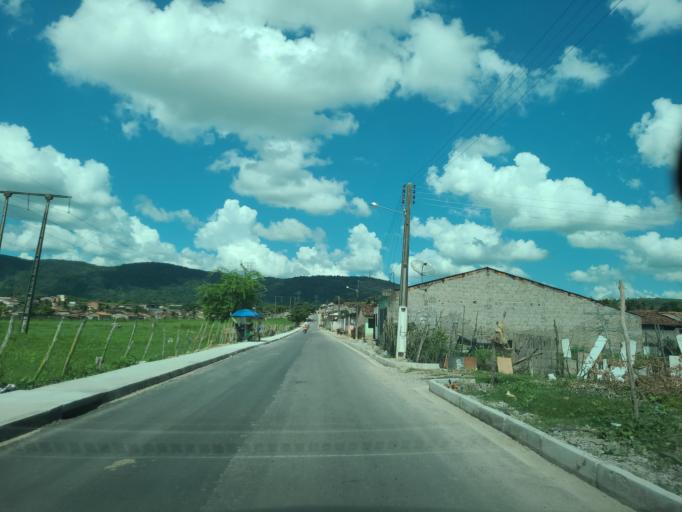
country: BR
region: Alagoas
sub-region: Uniao Dos Palmares
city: Uniao dos Palmares
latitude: -9.1574
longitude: -36.0193
